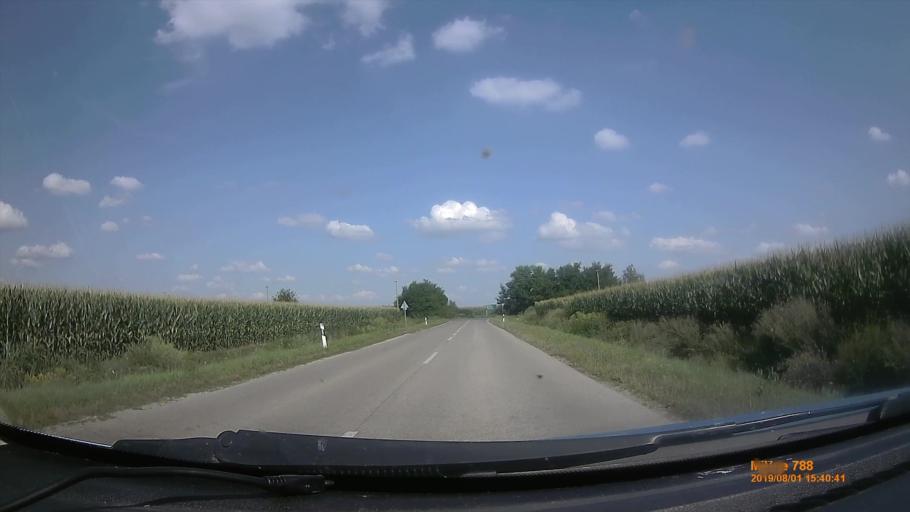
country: HU
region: Baranya
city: Szentlorinc
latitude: 45.9872
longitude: 17.9567
